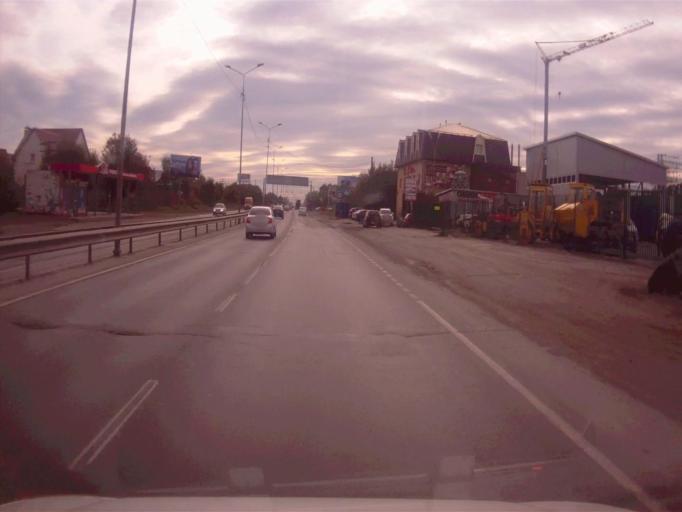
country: RU
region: Chelyabinsk
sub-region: Gorod Chelyabinsk
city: Chelyabinsk
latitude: 55.1114
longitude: 61.4103
